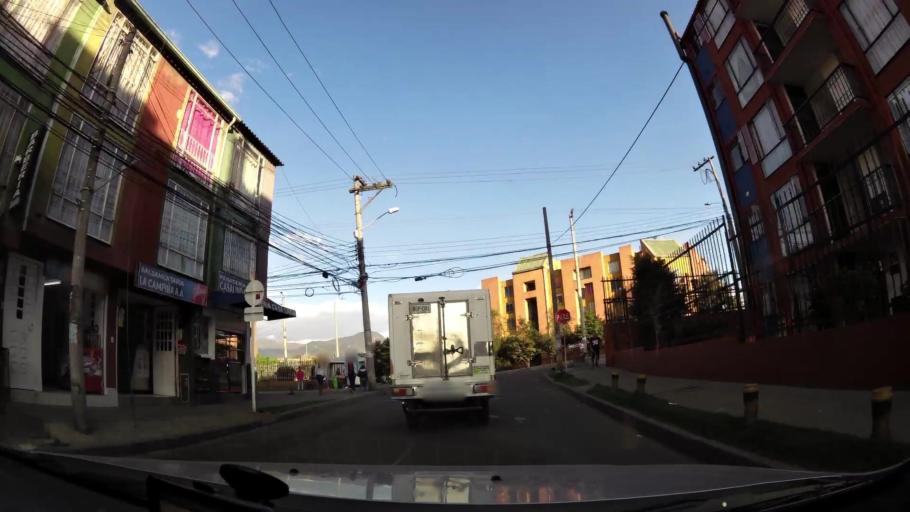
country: CO
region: Bogota D.C.
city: Bogota
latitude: 4.5682
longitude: -74.1433
